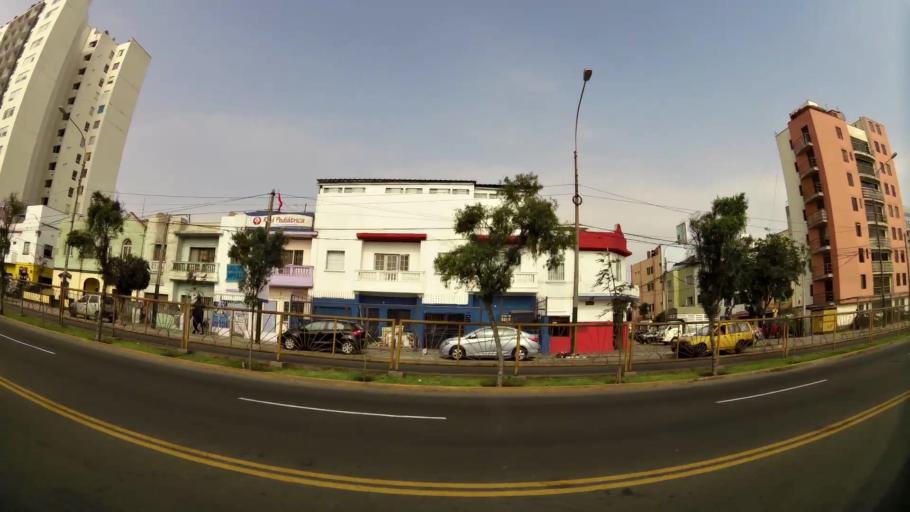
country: PE
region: Lima
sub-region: Lima
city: San Isidro
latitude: -12.0886
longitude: -77.0649
